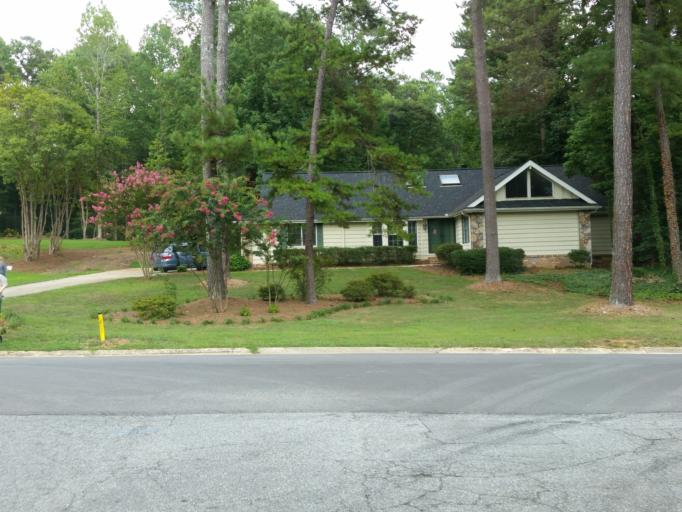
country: US
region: Georgia
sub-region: Fulton County
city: Sandy Springs
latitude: 33.9624
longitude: -84.4464
